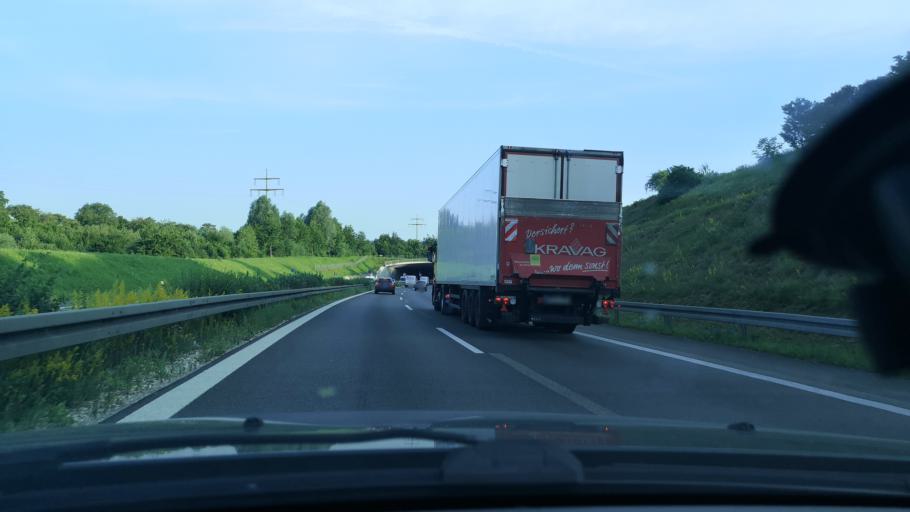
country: DE
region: Baden-Wuerttemberg
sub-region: Regierungsbezirk Stuttgart
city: Eislingen
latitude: 48.6832
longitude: 9.7038
